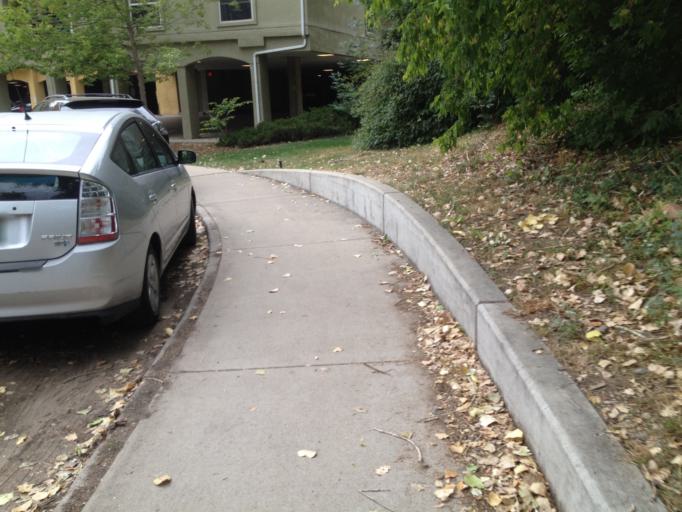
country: US
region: Colorado
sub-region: Boulder County
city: Boulder
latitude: 40.0107
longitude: -105.2631
